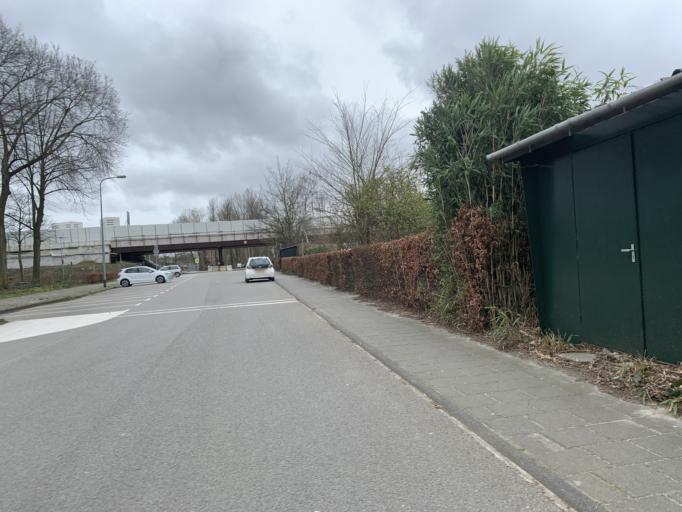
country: NL
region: Groningen
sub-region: Gemeente Groningen
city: Oosterpark
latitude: 53.2106
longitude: 6.5832
